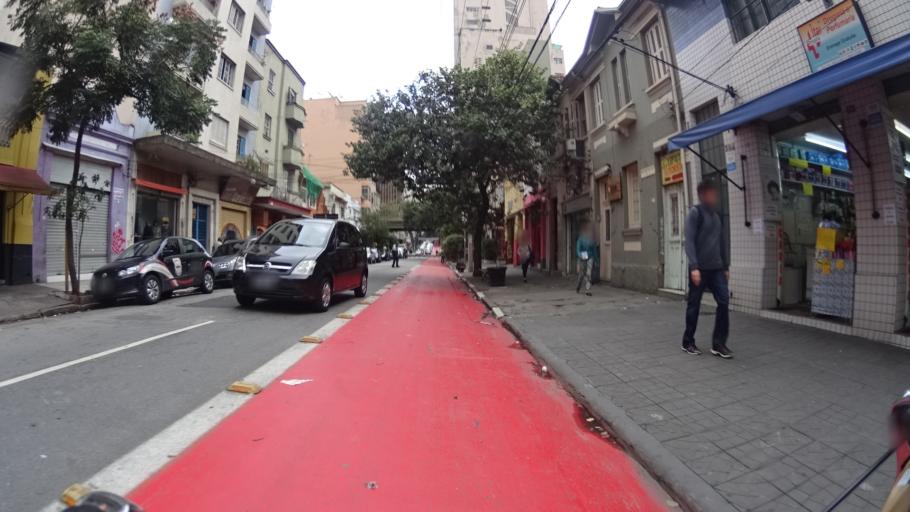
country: BR
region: Sao Paulo
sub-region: Sao Paulo
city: Sao Paulo
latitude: -23.5331
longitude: -46.6547
